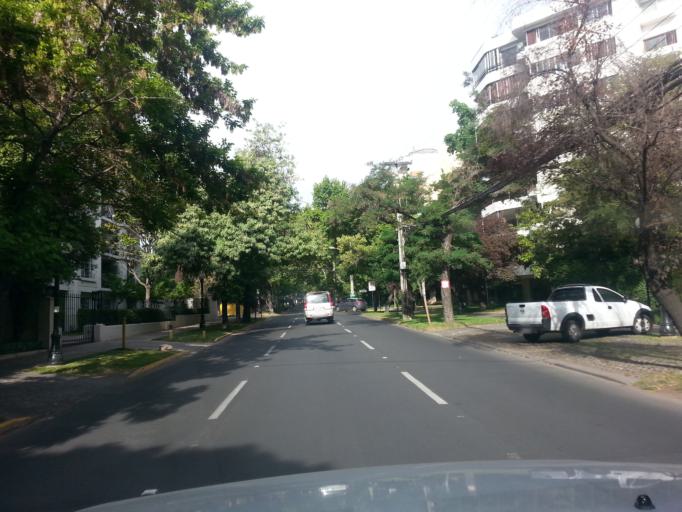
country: CL
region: Santiago Metropolitan
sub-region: Provincia de Santiago
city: Villa Presidente Frei, Nunoa, Santiago, Chile
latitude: -33.4255
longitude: -70.5963
